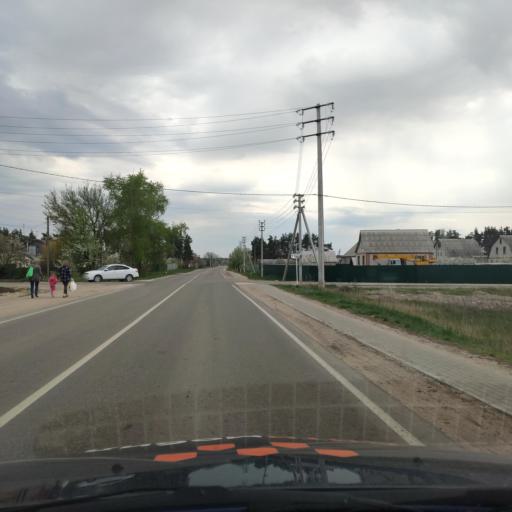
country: RU
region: Voronezj
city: Podgornoye
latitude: 51.8781
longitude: 39.1730
